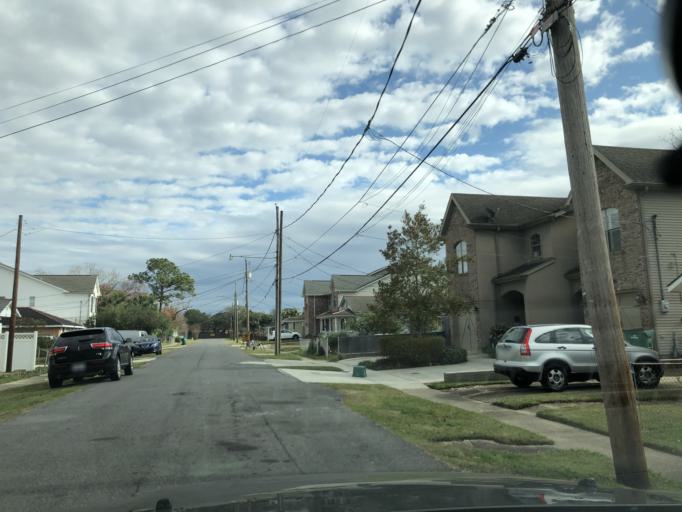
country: US
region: Louisiana
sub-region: Jefferson Parish
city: Metairie Terrace
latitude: 29.9792
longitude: -90.1663
